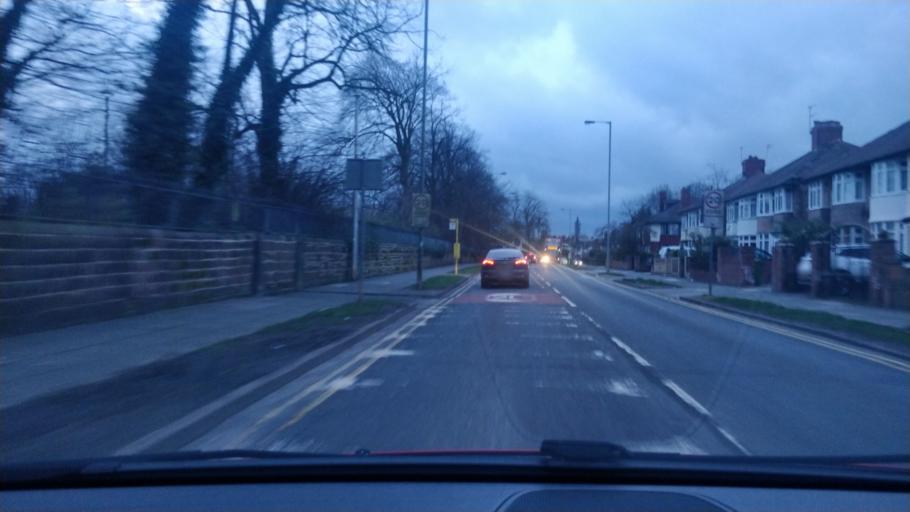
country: GB
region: England
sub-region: Knowsley
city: Knowsley
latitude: 53.4233
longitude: -2.8918
